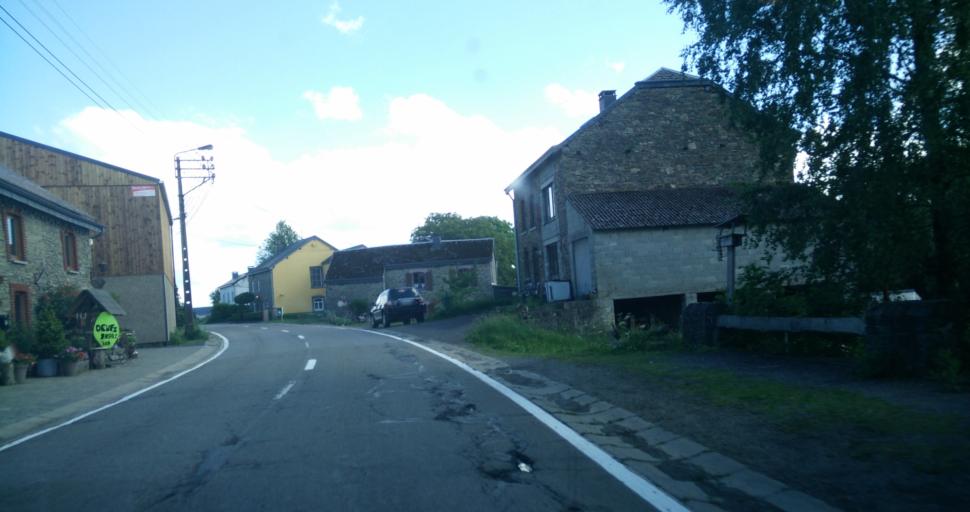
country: BE
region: Wallonia
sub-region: Province du Luxembourg
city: La Roche-en-Ardenne
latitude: 50.1761
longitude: 5.6664
